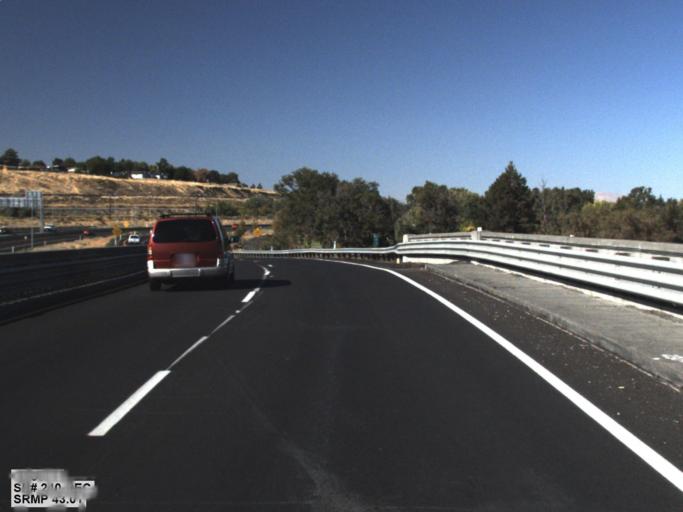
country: US
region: Washington
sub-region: Benton County
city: Kennewick
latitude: 46.2173
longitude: -119.1413
